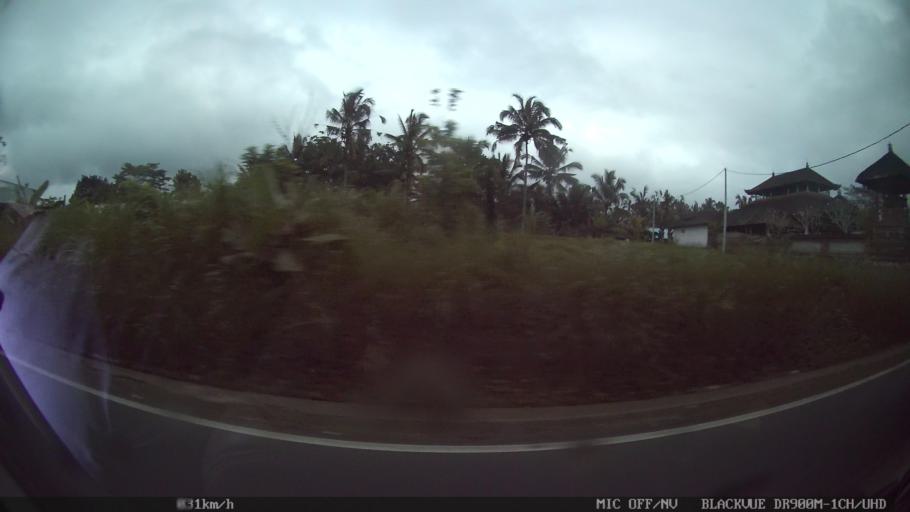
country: ID
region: Bali
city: Badung
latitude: -8.4233
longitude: 115.2450
